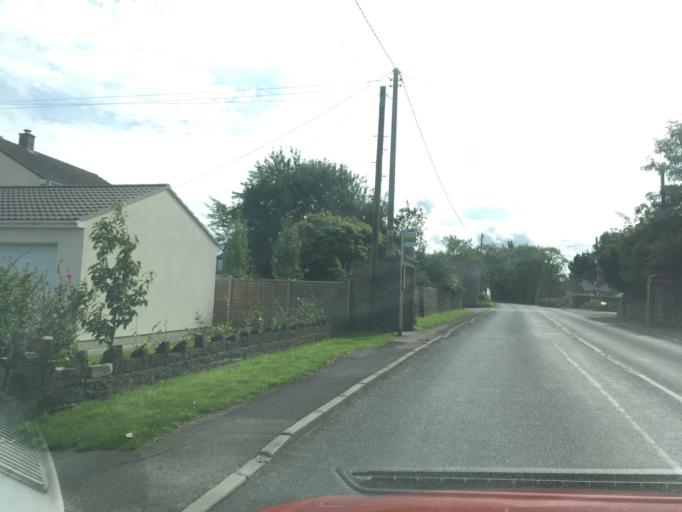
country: GB
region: England
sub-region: South Gloucestershire
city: Tytherington
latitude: 51.6008
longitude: -2.4399
